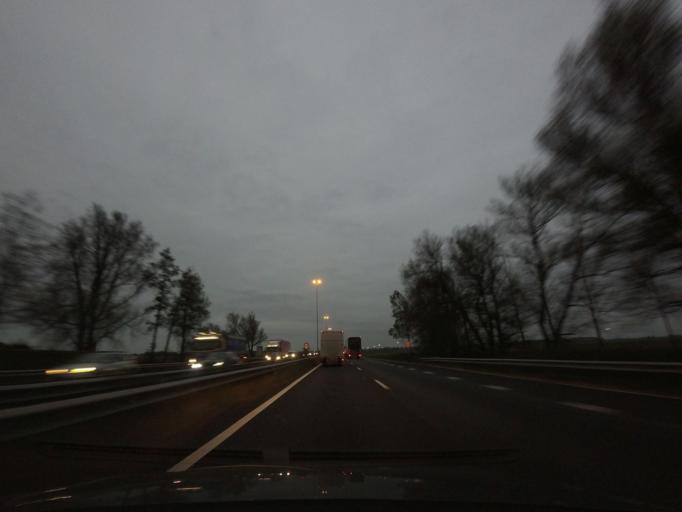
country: NL
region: North Brabant
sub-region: Gemeente Werkendam
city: Werkendam
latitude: 51.7983
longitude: 4.9309
